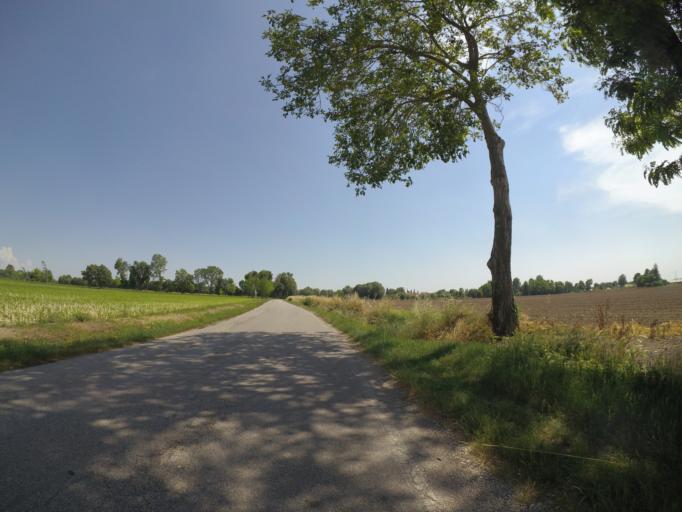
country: IT
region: Friuli Venezia Giulia
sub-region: Provincia di Udine
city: Camino al Tagliamento
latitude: 45.9470
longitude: 12.9397
